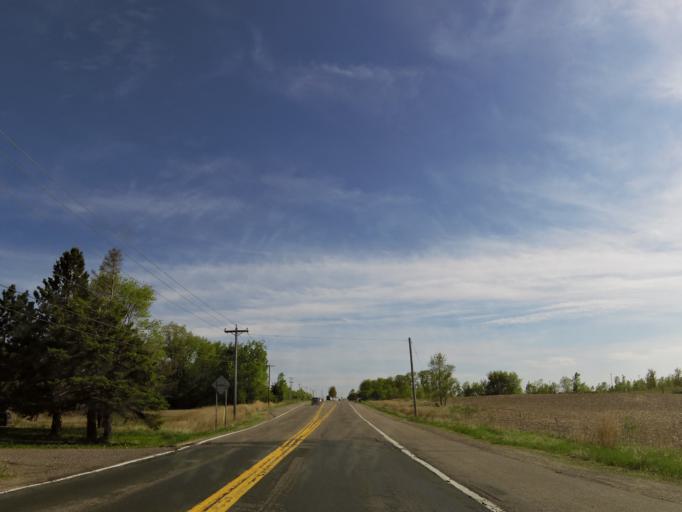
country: US
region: Minnesota
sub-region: Washington County
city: Oakdale
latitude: 45.0034
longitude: -92.9443
